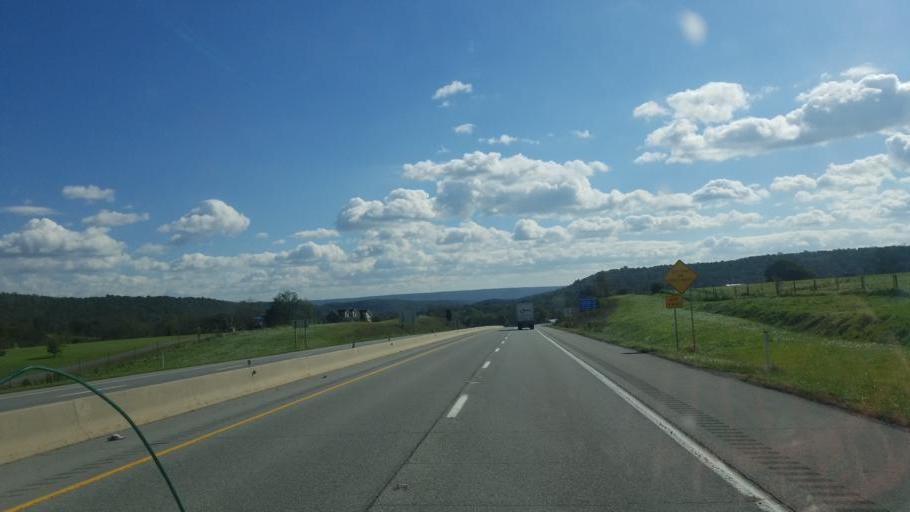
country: US
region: Pennsylvania
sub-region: Bedford County
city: Everett
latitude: 40.0221
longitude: -78.3561
